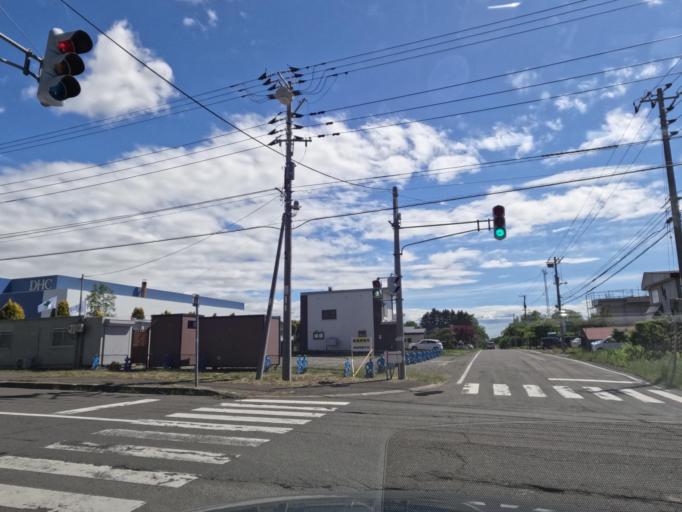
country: JP
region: Hokkaido
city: Kitahiroshima
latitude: 42.9984
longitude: 141.7237
